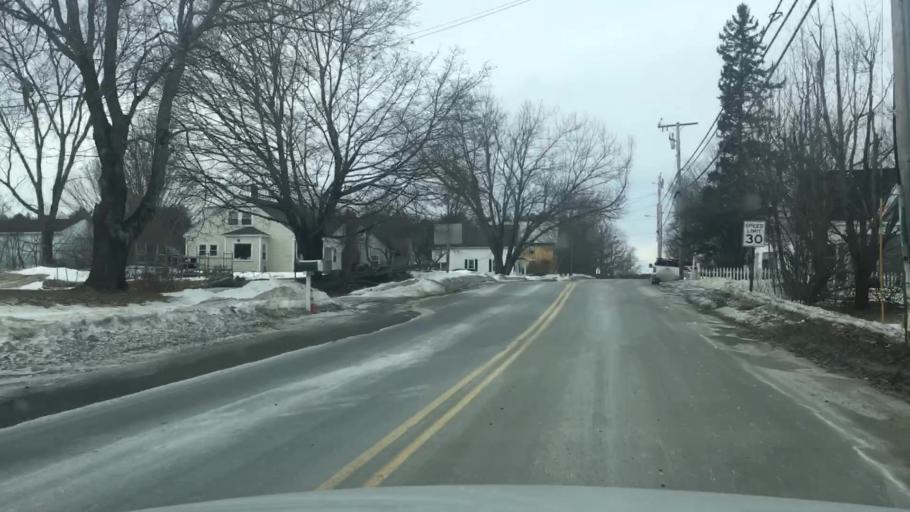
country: US
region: Maine
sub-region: Lincoln County
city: Whitefield
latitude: 44.2220
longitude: -69.5879
